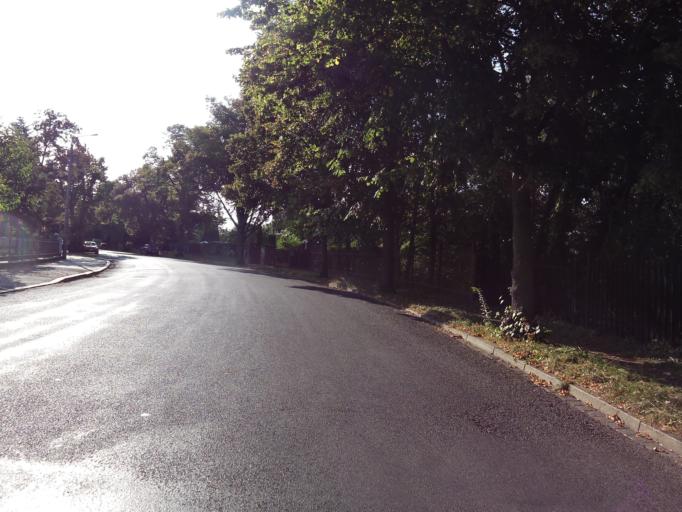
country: DE
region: Saxony
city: Leipzig
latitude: 51.3550
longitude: 12.3121
